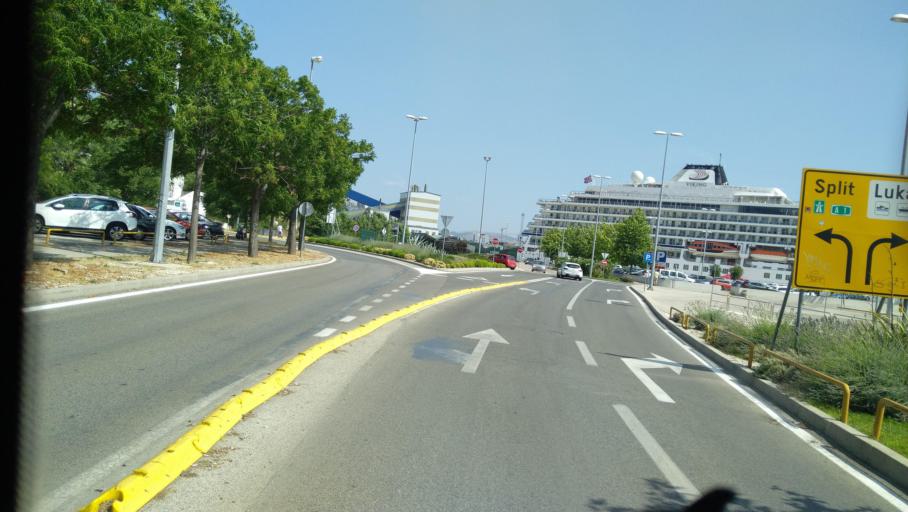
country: HR
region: Sibensko-Kniniska
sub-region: Grad Sibenik
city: Sibenik
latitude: 43.7309
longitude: 15.8948
